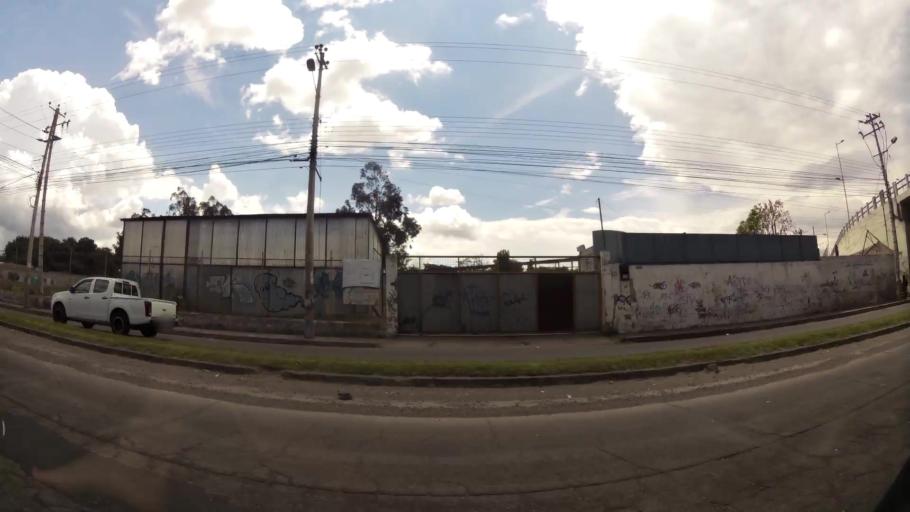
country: EC
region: Pichincha
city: Quito
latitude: -0.1044
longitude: -78.4275
